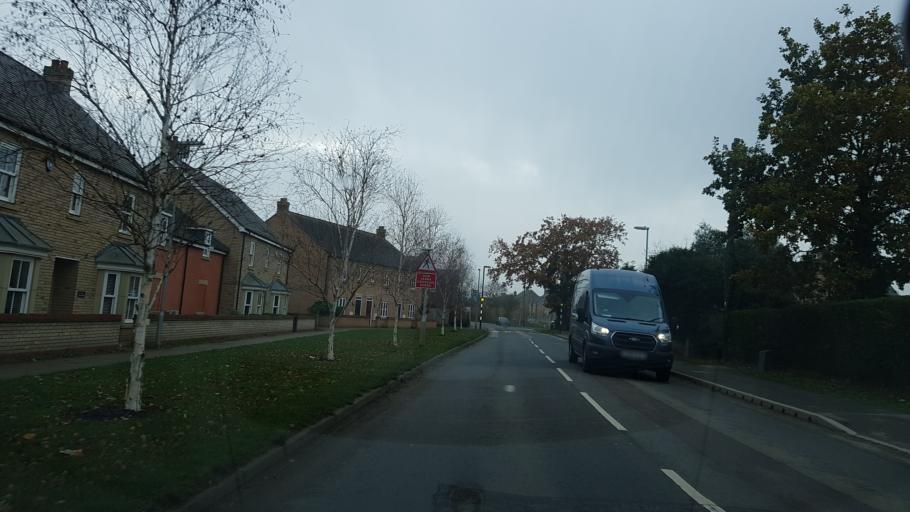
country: GB
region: England
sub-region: Central Bedfordshire
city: Biggleswade
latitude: 52.0978
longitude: -0.2495
